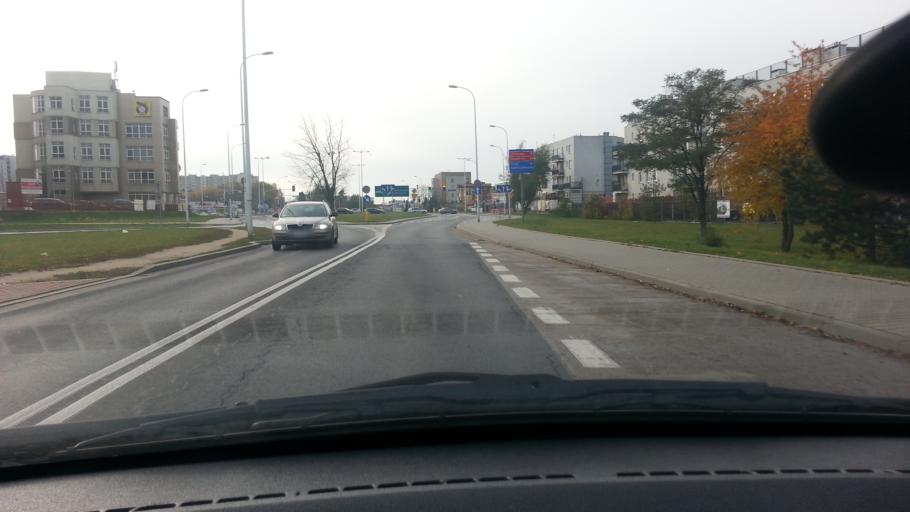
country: PL
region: Masovian Voivodeship
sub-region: Warszawa
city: Bemowo
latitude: 52.2413
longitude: 20.8968
